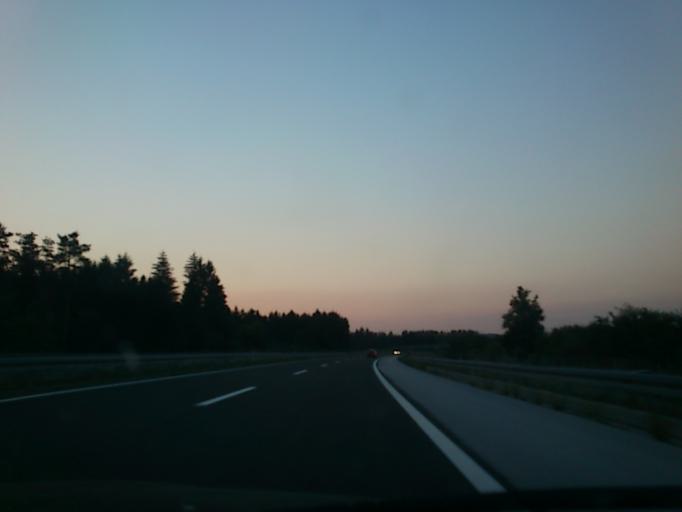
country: HR
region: Karlovacka
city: Ostarije
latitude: 45.2157
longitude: 15.2588
